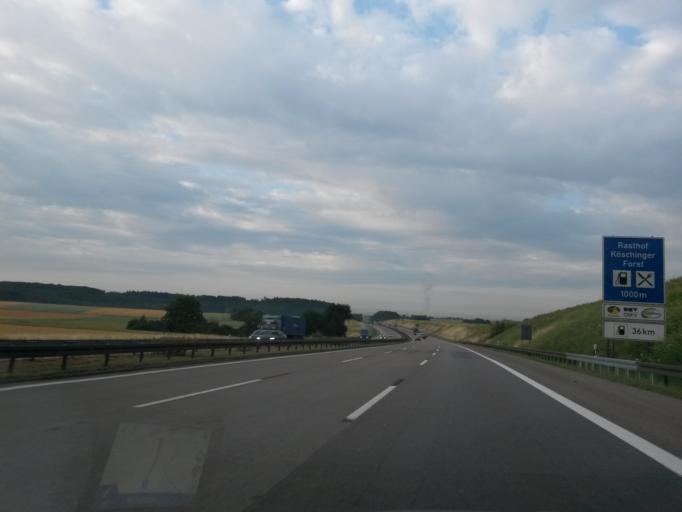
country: DE
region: Bavaria
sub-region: Upper Bavaria
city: Stammham
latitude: 48.8515
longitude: 11.4646
